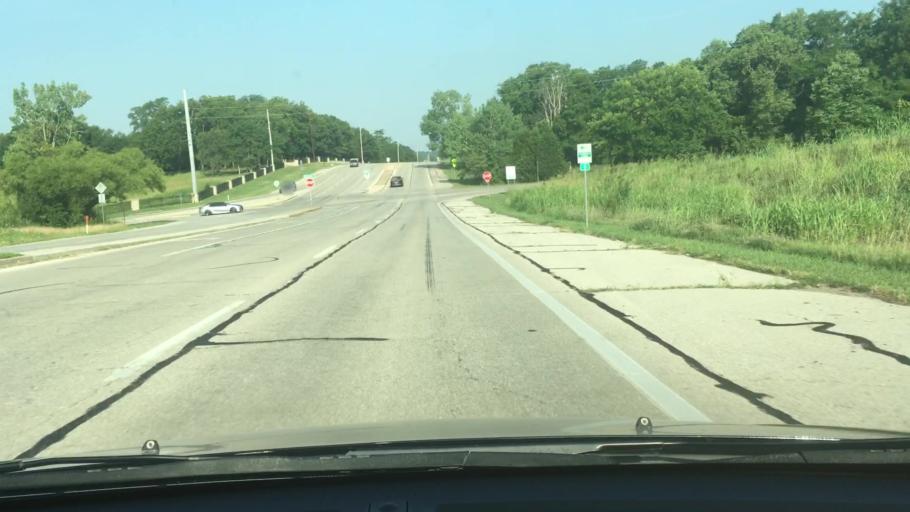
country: US
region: Missouri
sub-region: Jackson County
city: Grandview
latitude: 38.8847
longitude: -94.4747
